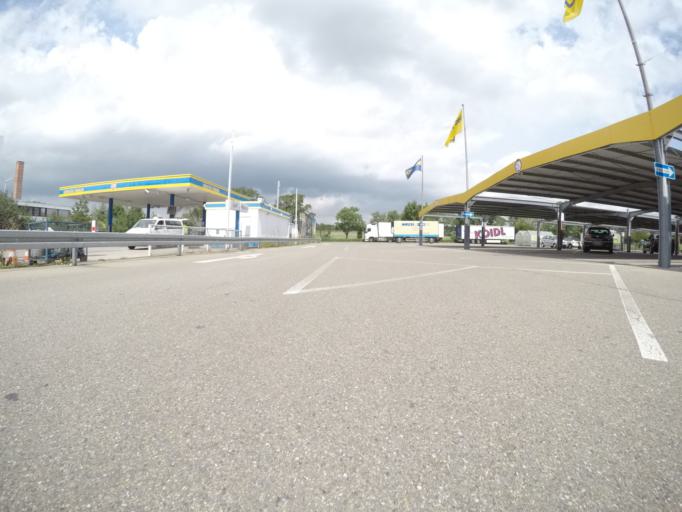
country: DE
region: Baden-Wuerttemberg
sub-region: Regierungsbezirk Stuttgart
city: Korntal
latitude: 48.8276
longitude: 9.1089
